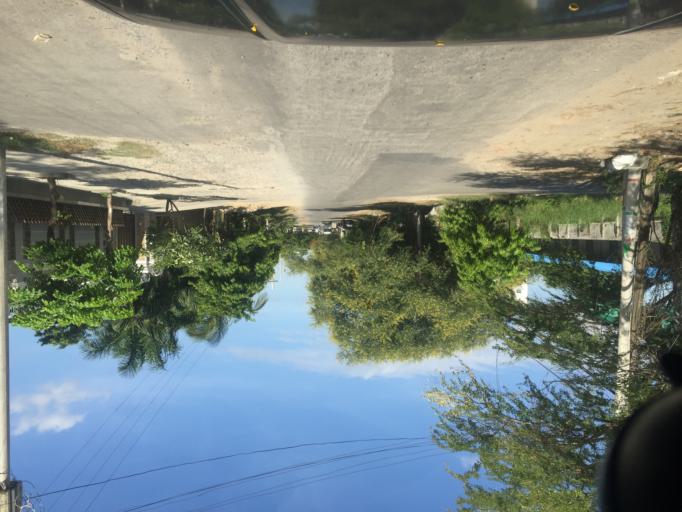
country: MM
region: Mandalay
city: Mandalay
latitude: 21.9536
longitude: 96.1078
